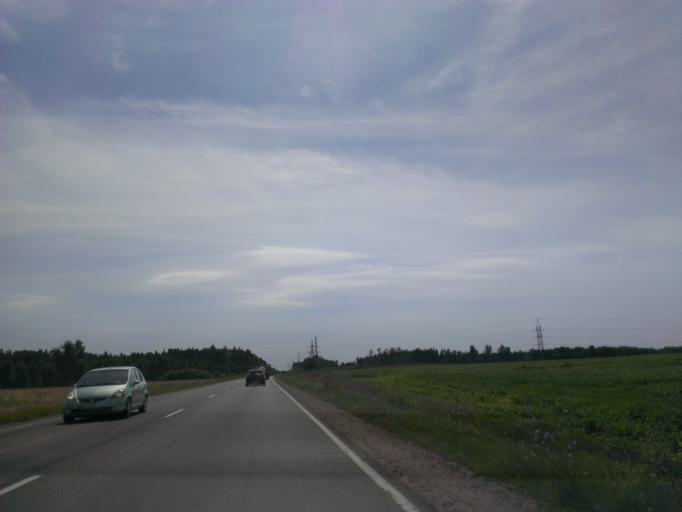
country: LV
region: Salaspils
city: Salaspils
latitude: 56.8809
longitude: 24.4077
